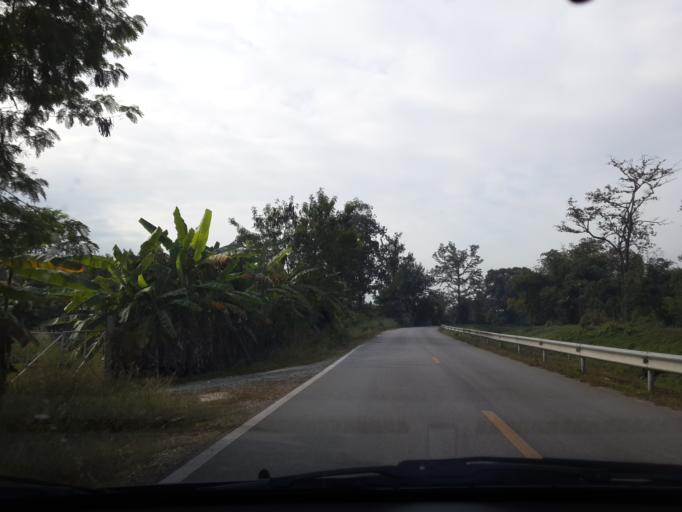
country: TH
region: Chiang Mai
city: San Sai
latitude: 18.8981
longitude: 99.0375
